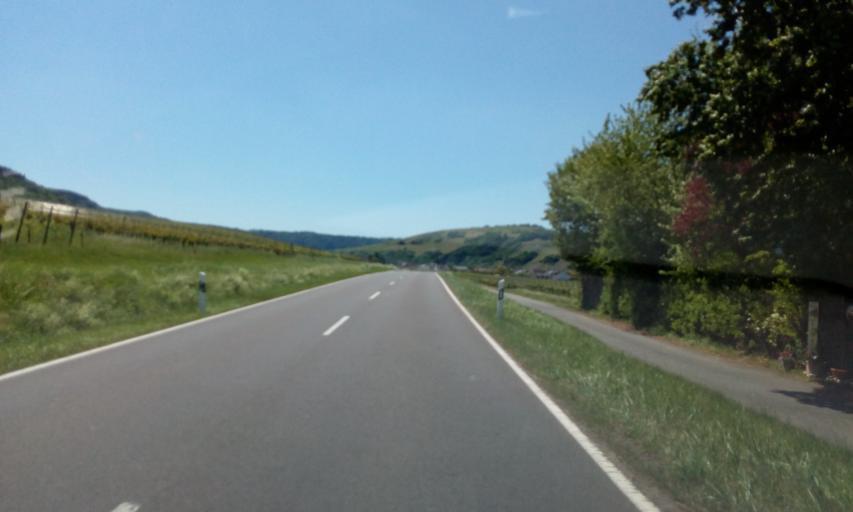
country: DE
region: Rheinland-Pfalz
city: Kesten
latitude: 49.8946
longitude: 6.9622
